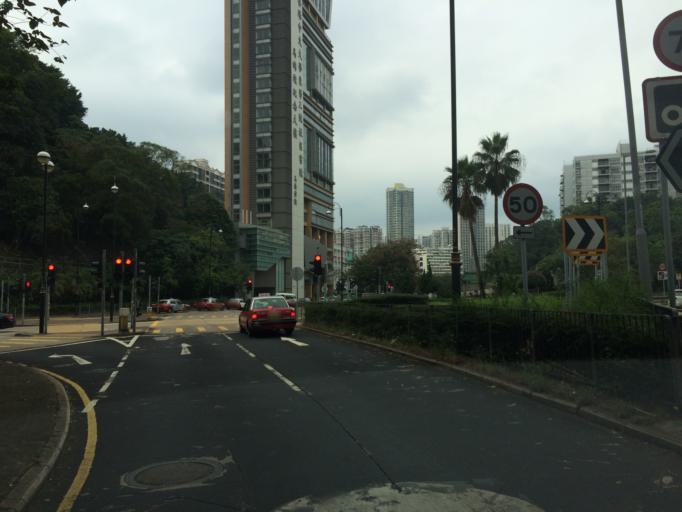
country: HK
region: Kowloon City
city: Kowloon
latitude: 22.3119
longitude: 114.1767
